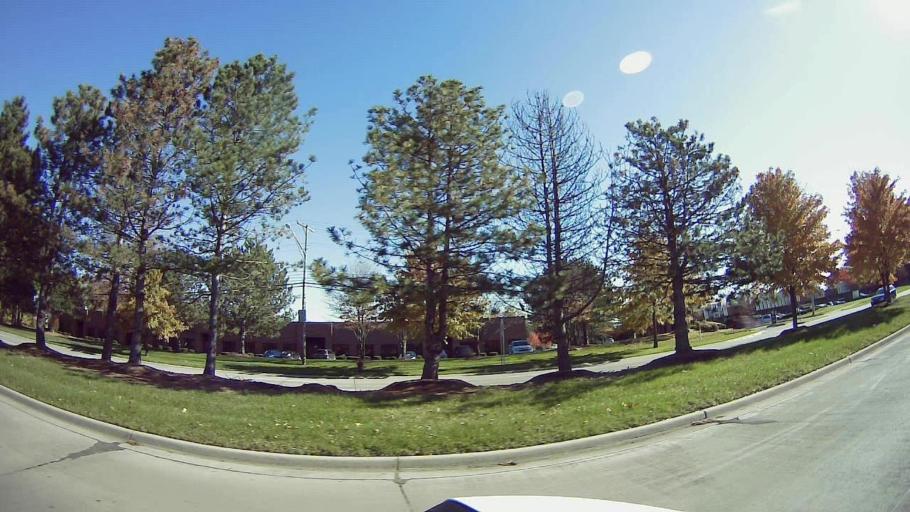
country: US
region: Michigan
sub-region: Oakland County
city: Southfield
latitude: 42.4476
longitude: -83.2596
